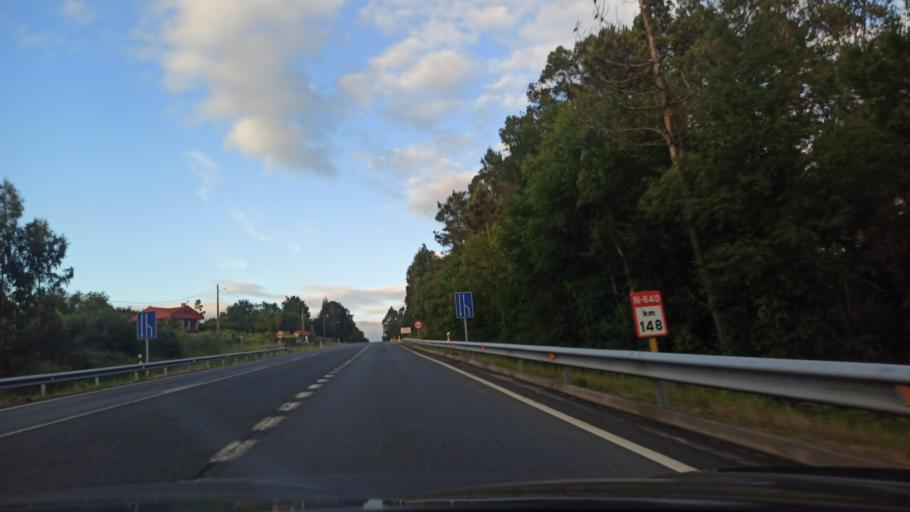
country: ES
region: Galicia
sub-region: Provincia da Coruna
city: Santiso
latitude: 42.7639
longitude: -8.0105
